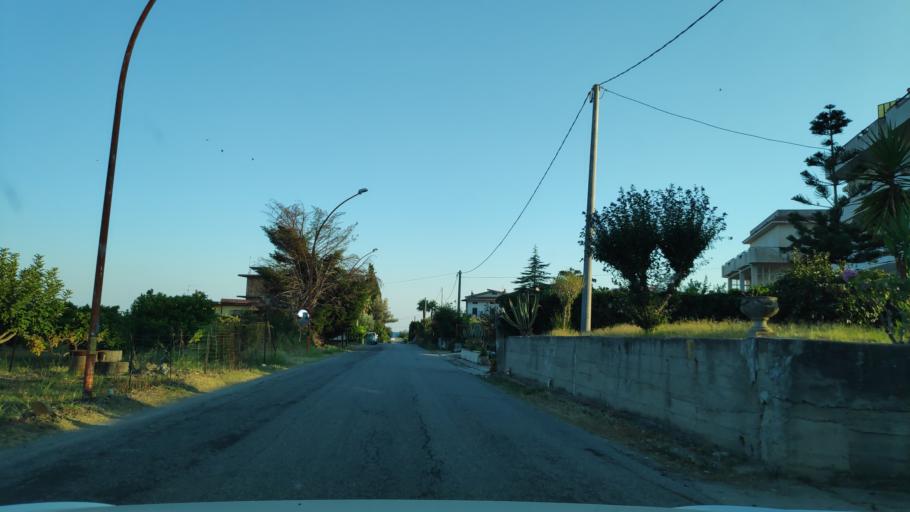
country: IT
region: Calabria
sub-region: Provincia di Reggio Calabria
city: Caulonia Marina
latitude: 38.3609
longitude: 16.4854
